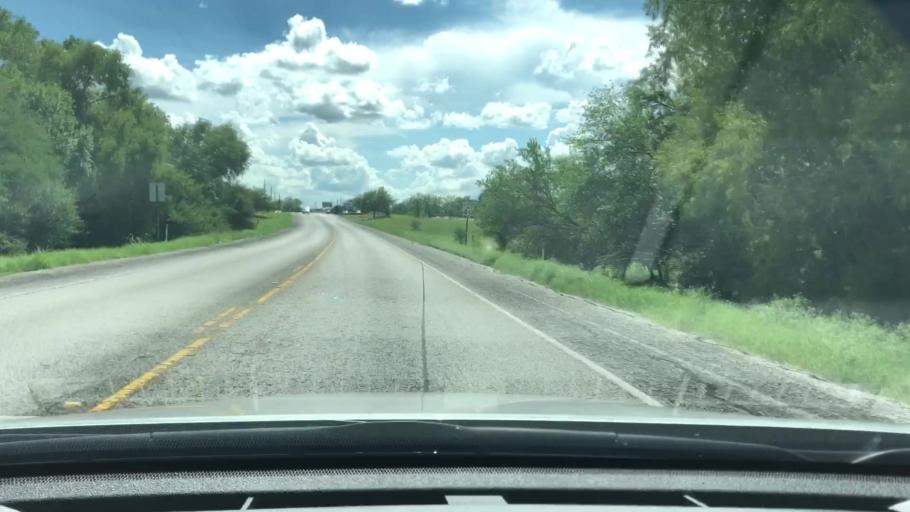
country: US
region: Texas
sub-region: Bexar County
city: Converse
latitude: 29.5233
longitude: -98.3122
